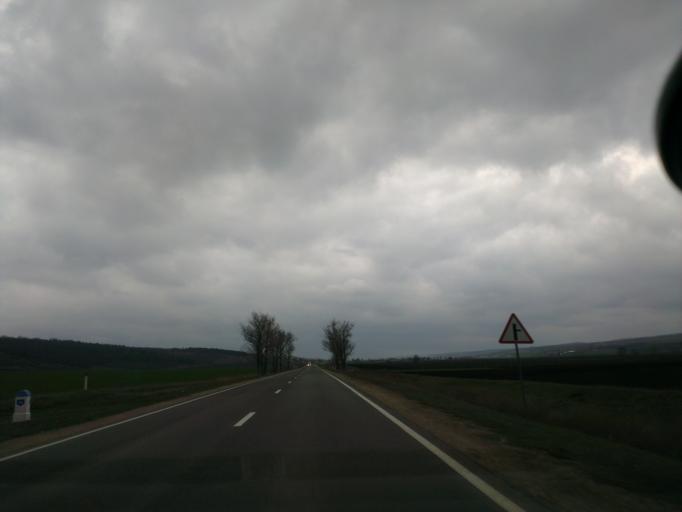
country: MD
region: Hincesti
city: Hincesti
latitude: 46.7298
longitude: 28.6592
